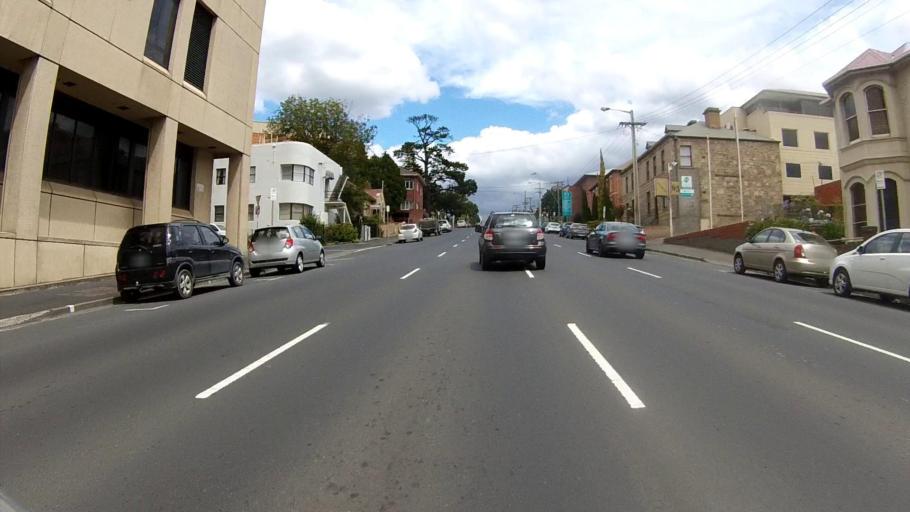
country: AU
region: Tasmania
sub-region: Hobart
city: Hobart
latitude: -42.8865
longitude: 147.3271
